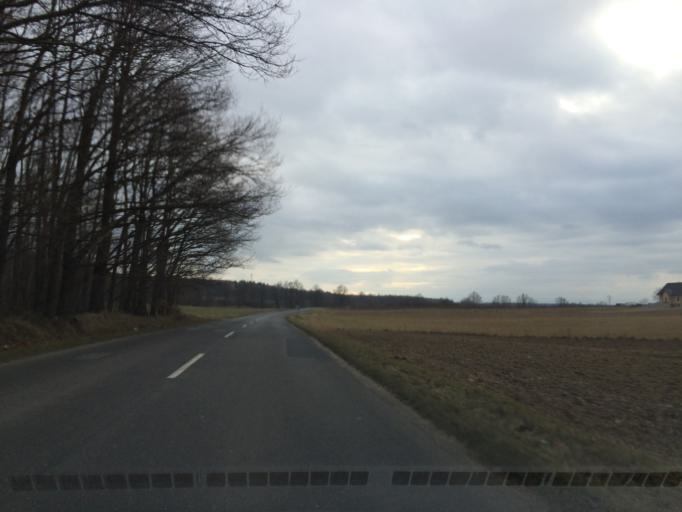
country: PL
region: Lower Silesian Voivodeship
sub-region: Powiat lwowecki
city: Lwowek Slaski
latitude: 51.1839
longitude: 15.5663
